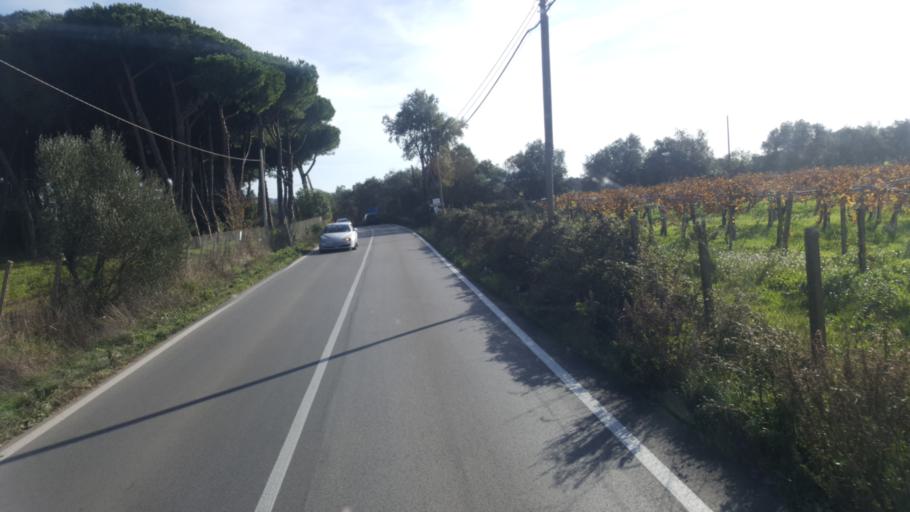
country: IT
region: Latium
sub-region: Citta metropolitana di Roma Capitale
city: Mantiglia di Ardea
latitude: 41.6851
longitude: 12.6119
